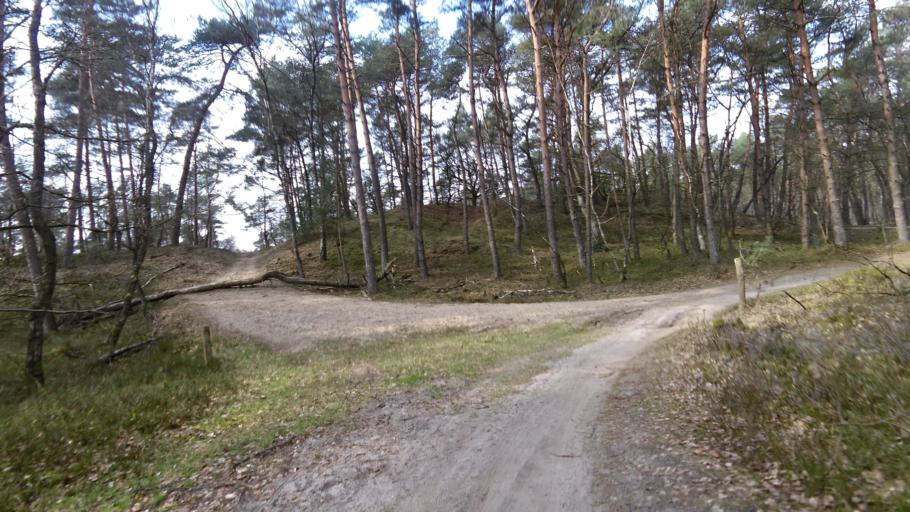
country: NL
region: Gelderland
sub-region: Gemeente Ede
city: Otterlo
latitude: 52.0808
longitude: 5.7445
